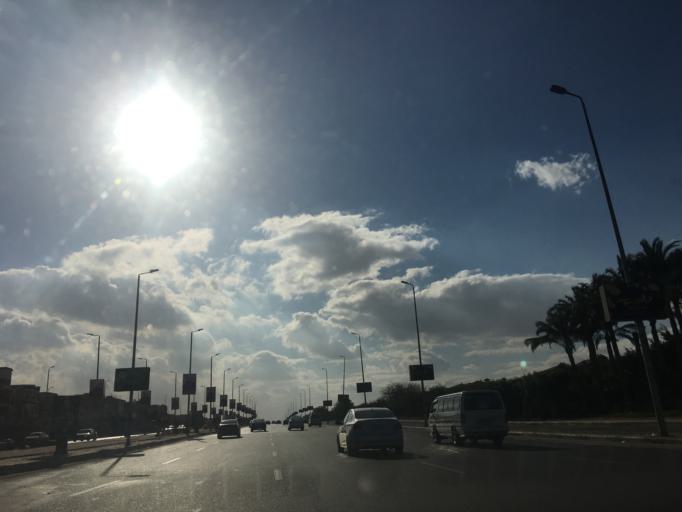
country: EG
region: Muhafazat al Qalyubiyah
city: Al Khankah
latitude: 30.0220
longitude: 31.4521
